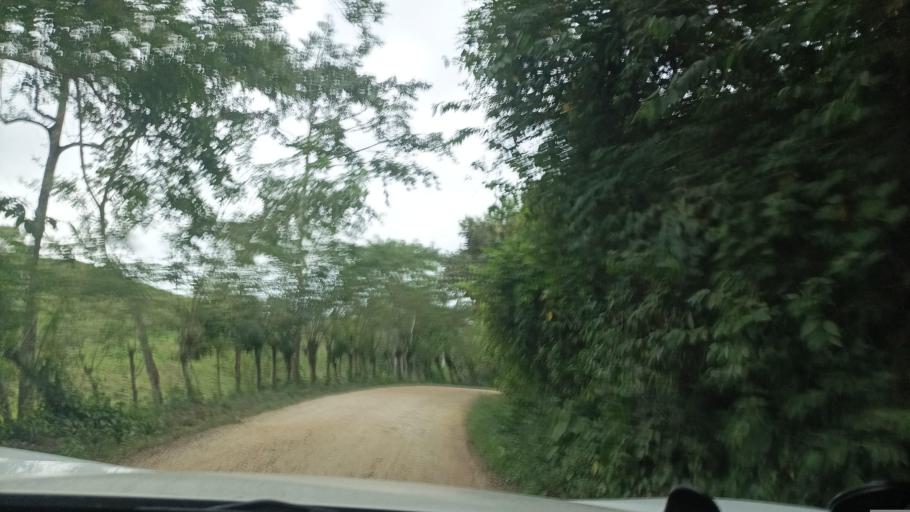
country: MX
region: Veracruz
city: Hidalgotitlan
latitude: 17.6050
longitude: -94.5275
